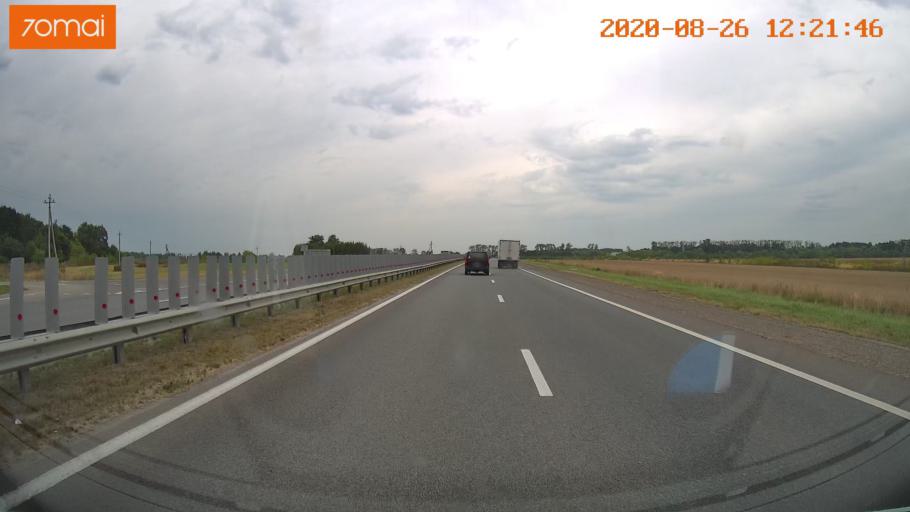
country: RU
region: Rjazan
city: Murmino
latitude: 54.5015
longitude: 39.9536
